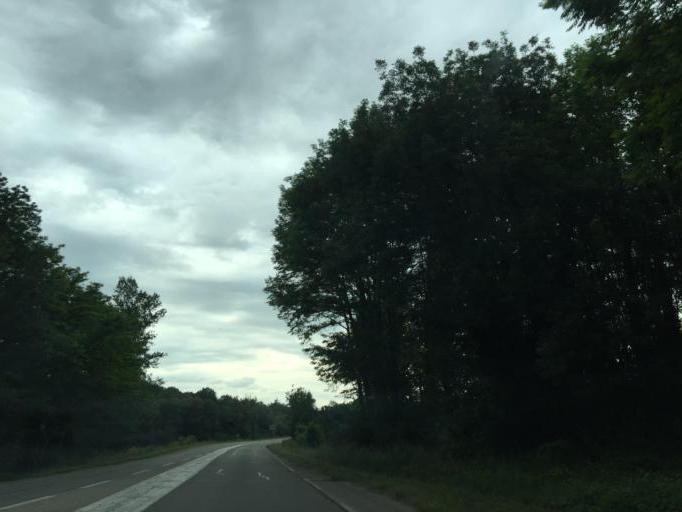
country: FR
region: Rhone-Alpes
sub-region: Departement de l'Isere
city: Romagnieu
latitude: 45.5707
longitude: 5.6578
